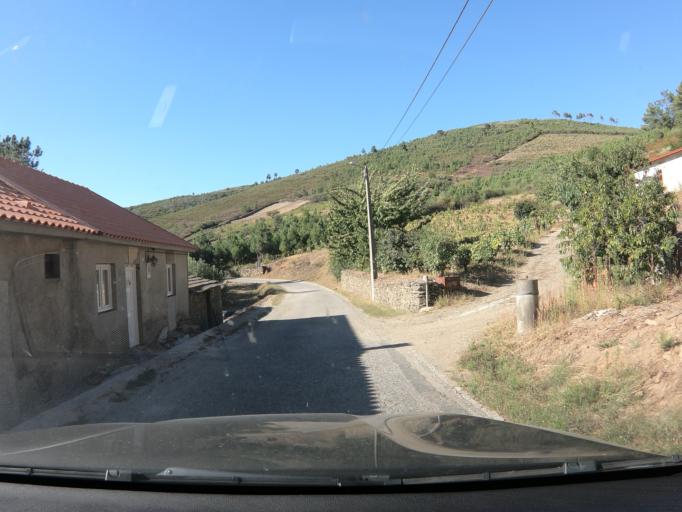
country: PT
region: Vila Real
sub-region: Sabrosa
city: Vilela
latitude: 41.2245
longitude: -7.5820
